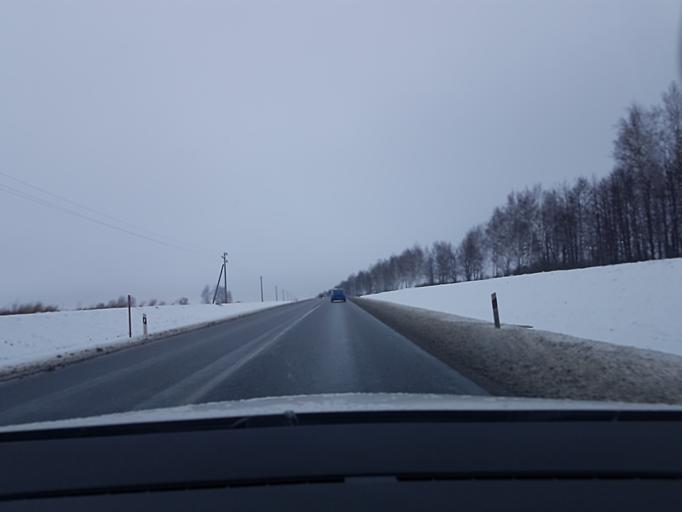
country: RU
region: Moskovskaya
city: Ozherel'ye
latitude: 54.7311
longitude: 38.2630
